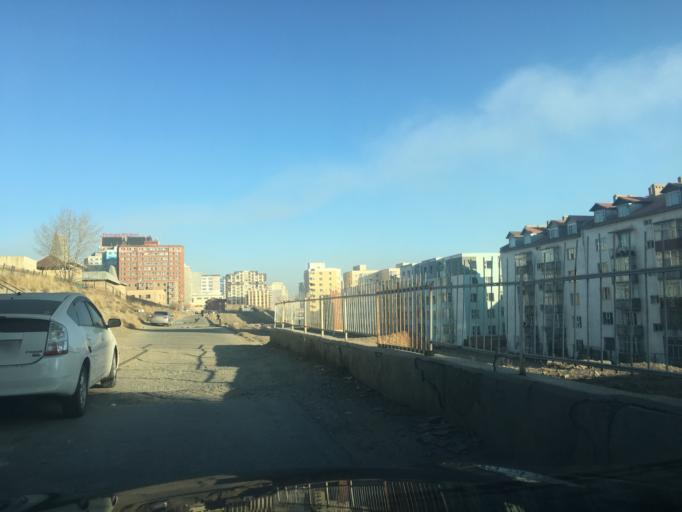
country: MN
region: Ulaanbaatar
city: Ulaanbaatar
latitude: 47.9172
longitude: 106.8768
